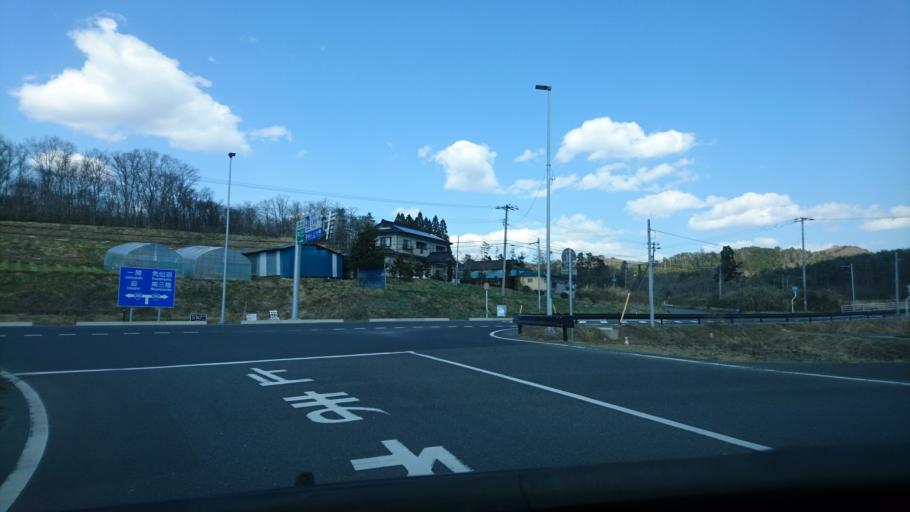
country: JP
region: Miyagi
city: Wakuya
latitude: 38.7085
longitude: 141.3277
